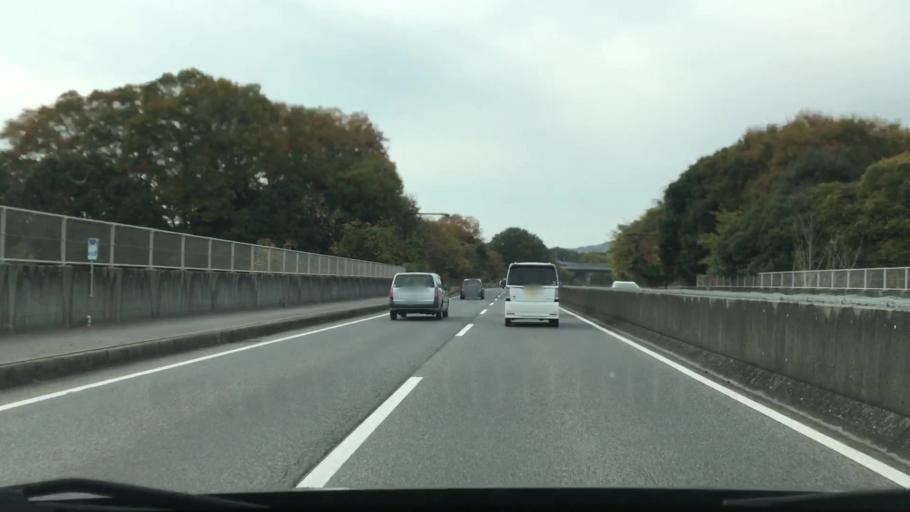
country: JP
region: Yamaguchi
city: Kudamatsu
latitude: 34.0308
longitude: 131.9183
